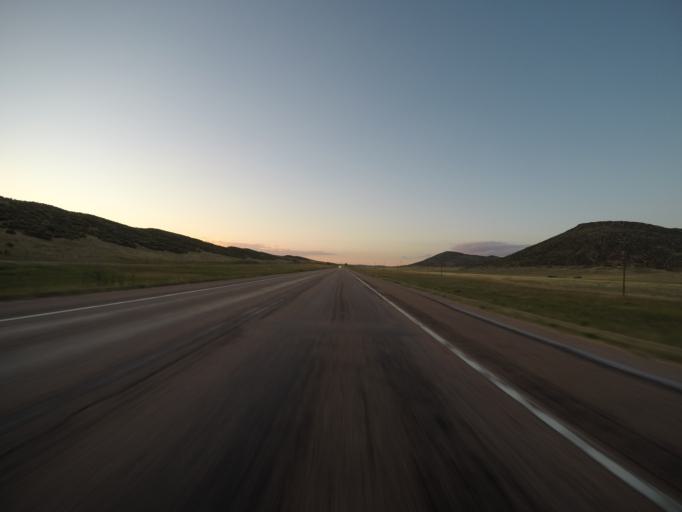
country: US
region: Colorado
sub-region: Larimer County
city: Laporte
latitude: 40.7333
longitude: -105.1712
